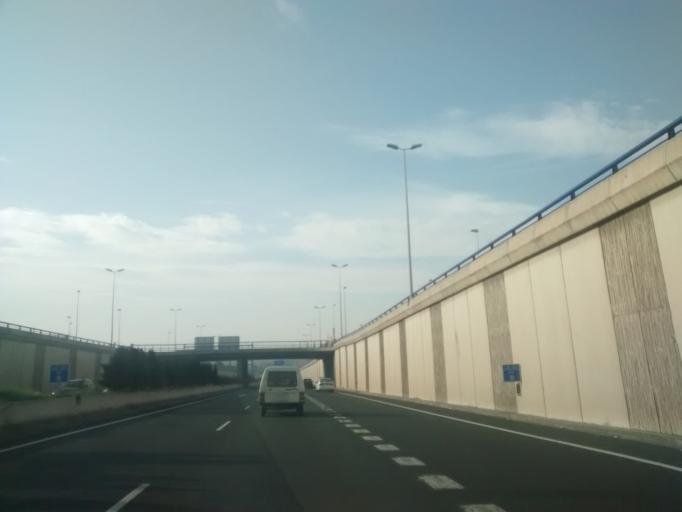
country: ES
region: La Rioja
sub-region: Provincia de La Rioja
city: Logrono
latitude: 42.4538
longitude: -2.4398
